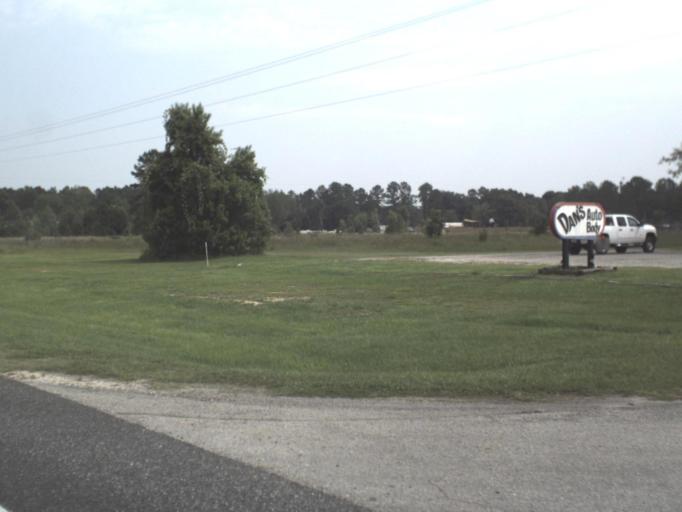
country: US
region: Florida
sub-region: Levy County
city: Williston
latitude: 29.3839
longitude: -82.4251
